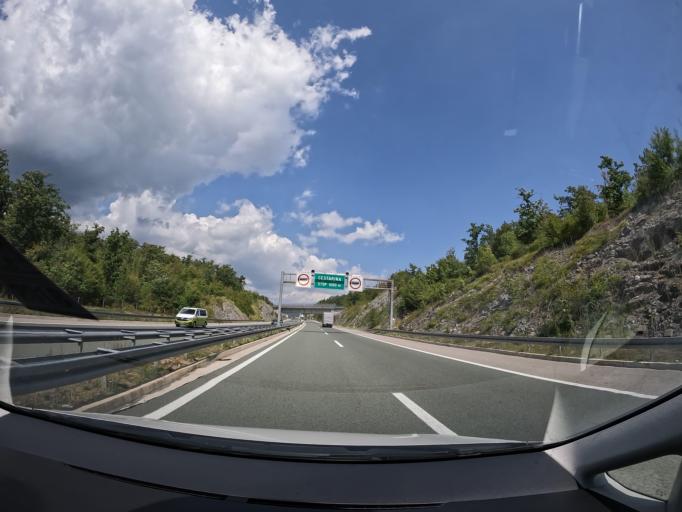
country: HR
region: Primorsko-Goranska
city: Matulji
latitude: 45.4473
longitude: 14.2728
